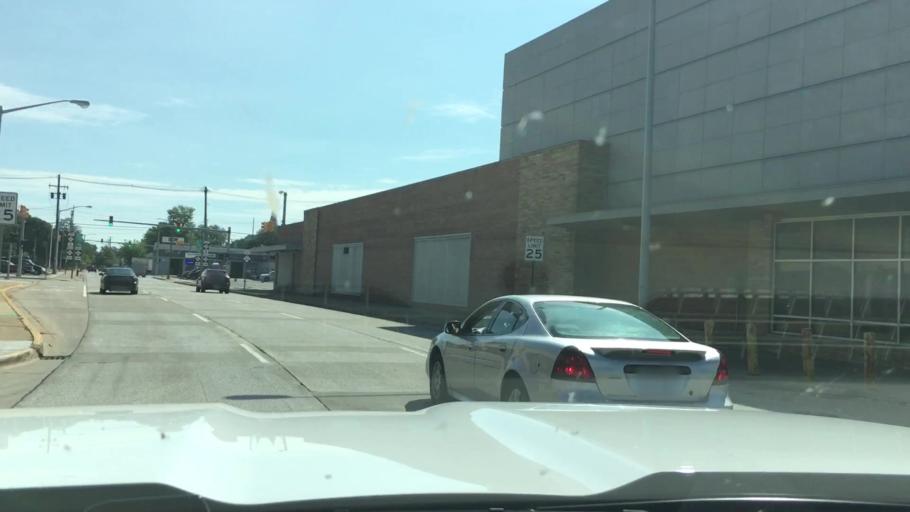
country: US
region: Michigan
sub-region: Bay County
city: Bay City
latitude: 43.5952
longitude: -83.8905
